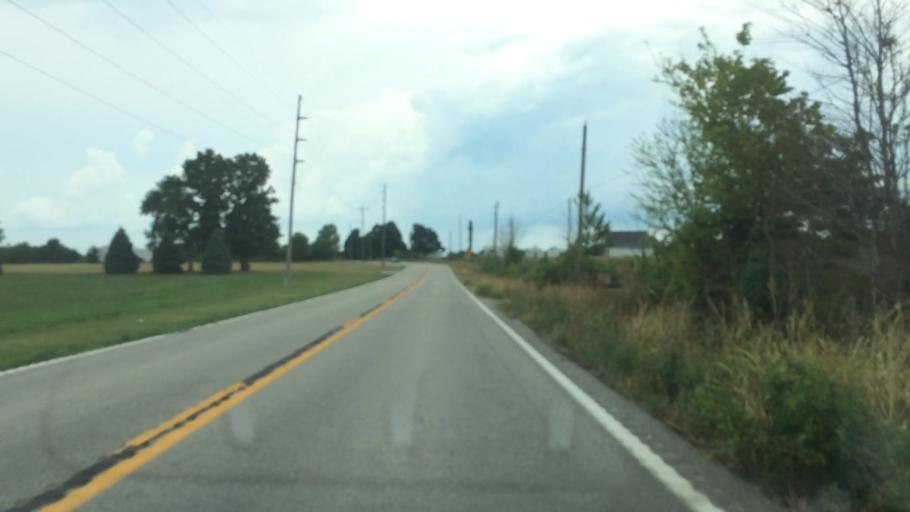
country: US
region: Missouri
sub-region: Greene County
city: Strafford
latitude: 37.2501
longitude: -93.1354
